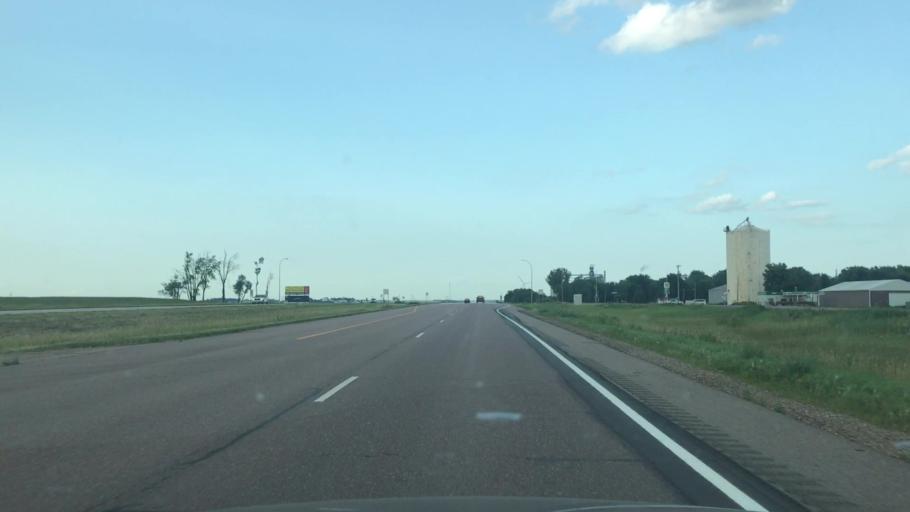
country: US
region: Minnesota
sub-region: Nobles County
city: Worthington
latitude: 43.6981
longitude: -95.4723
